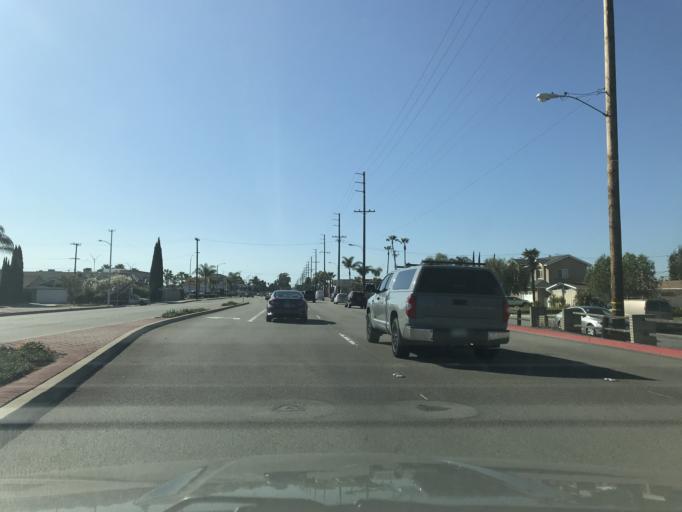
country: US
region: California
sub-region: Orange County
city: Huntington Beach
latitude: 33.6723
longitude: -117.9675
